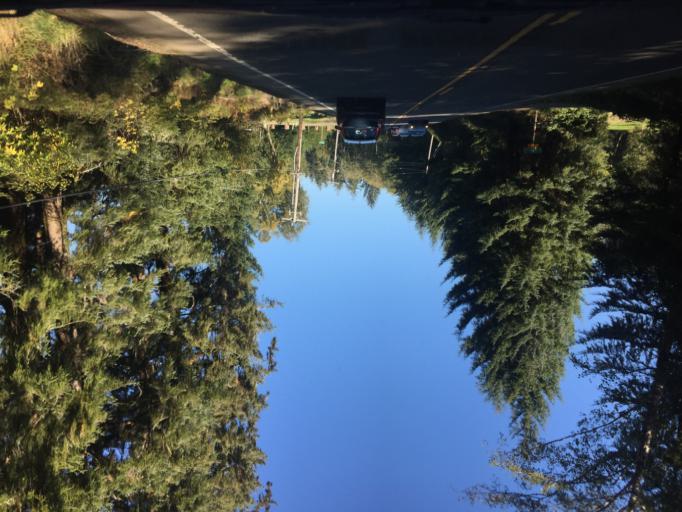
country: US
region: Oregon
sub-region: Clatsop County
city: Cannon Beach
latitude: 45.9054
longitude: -123.8779
